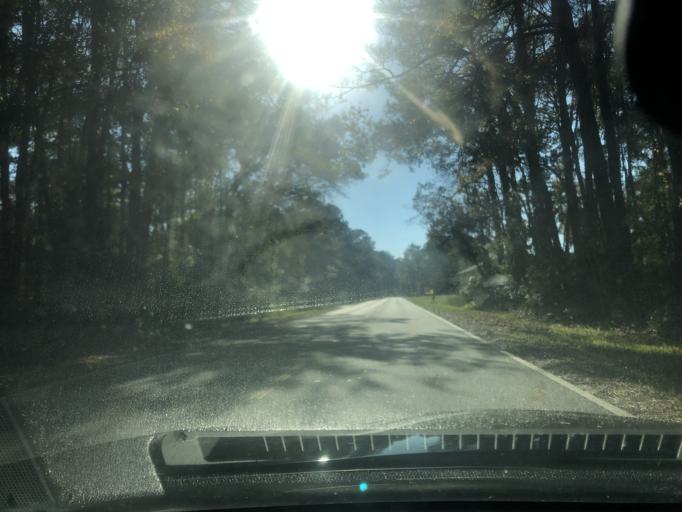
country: US
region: Florida
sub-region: Citrus County
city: Homosassa Springs
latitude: 28.8080
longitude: -82.5717
